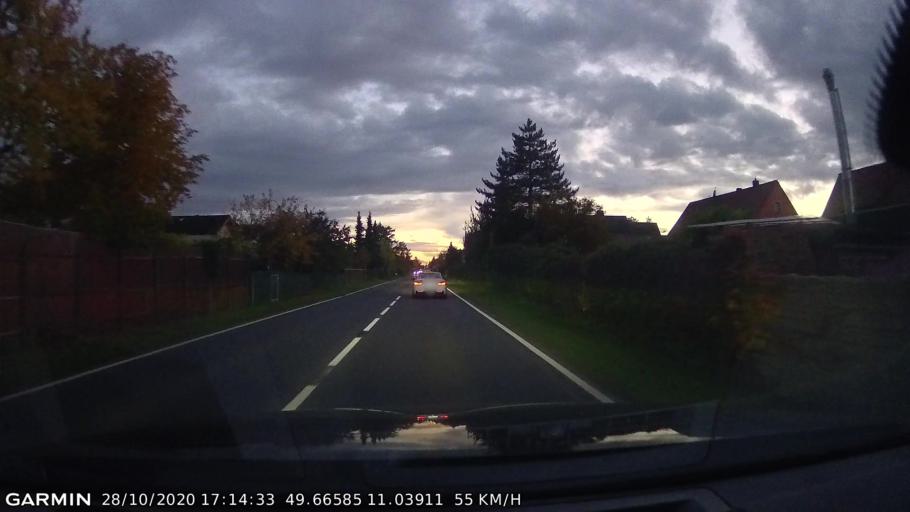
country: DE
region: Bavaria
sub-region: Regierungsbezirk Mittelfranken
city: Baiersdorf
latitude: 49.6658
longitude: 11.0391
